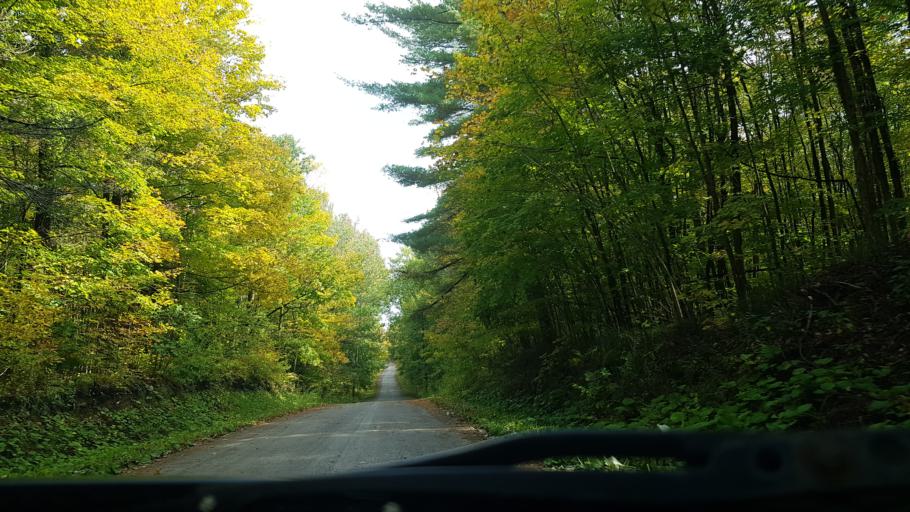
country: CA
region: Ontario
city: Orillia
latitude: 44.6754
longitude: -79.0898
